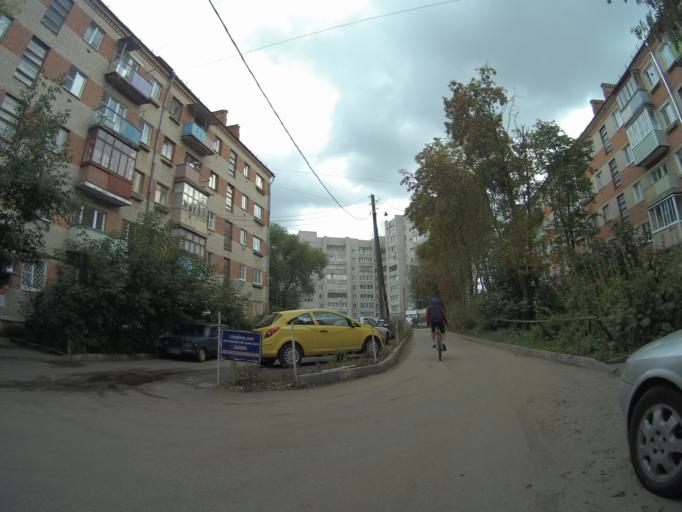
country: RU
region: Vladimir
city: Vladimir
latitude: 56.1122
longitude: 40.3547
